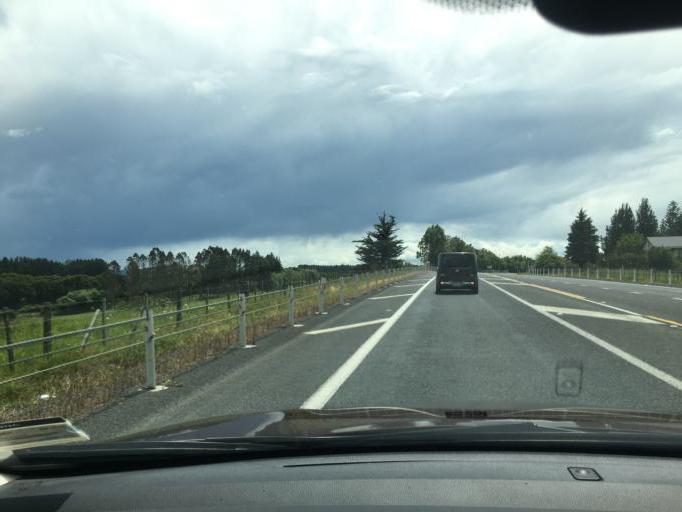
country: NZ
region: Waikato
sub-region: Waipa District
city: Cambridge
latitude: -37.9306
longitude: 175.3116
